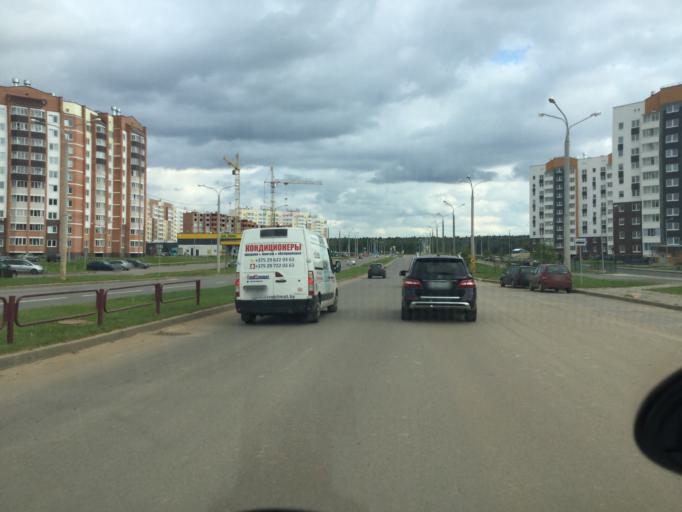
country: BY
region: Vitebsk
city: Vitebsk
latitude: 55.1643
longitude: 30.2715
